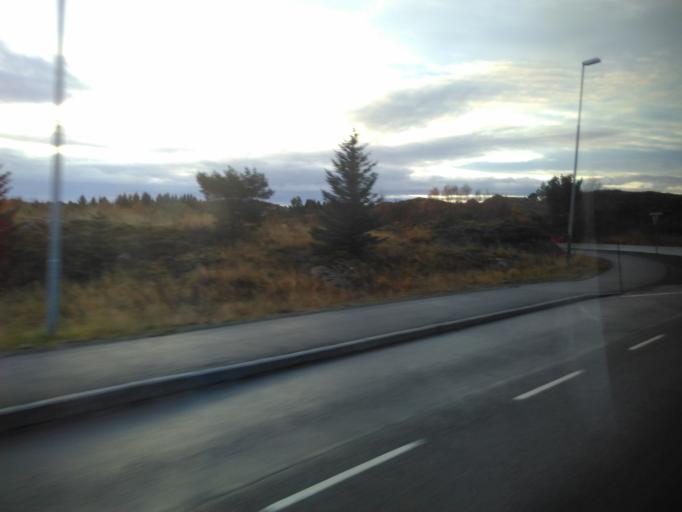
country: NO
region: Sor-Trondelag
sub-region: Froya
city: Sistranda
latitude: 63.6479
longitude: 8.8234
